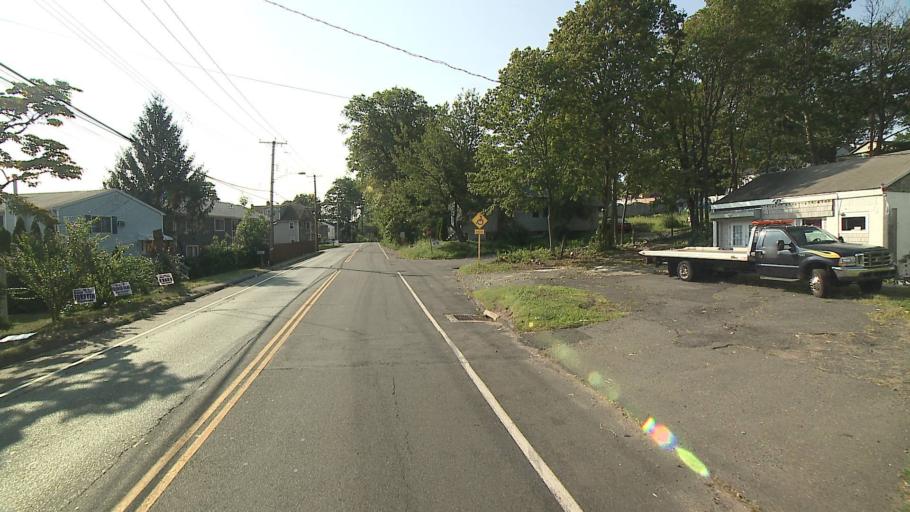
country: US
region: Connecticut
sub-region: New Haven County
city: West Haven
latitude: 41.3010
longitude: -72.9628
